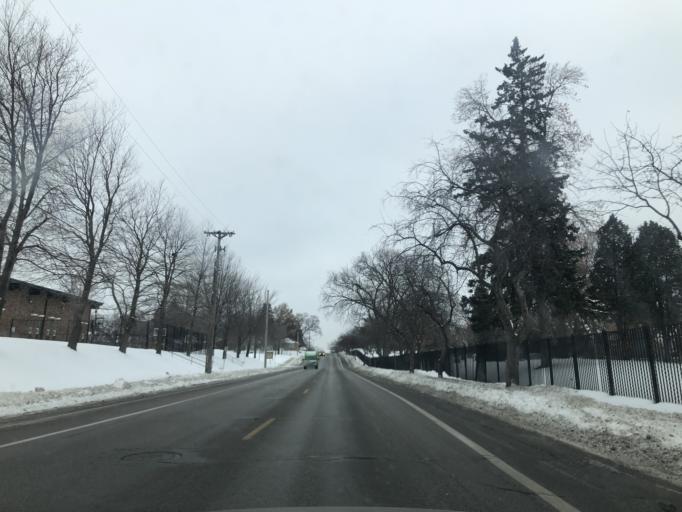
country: US
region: Minnesota
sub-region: Anoka County
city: Columbia Heights
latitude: 45.0240
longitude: -93.2993
